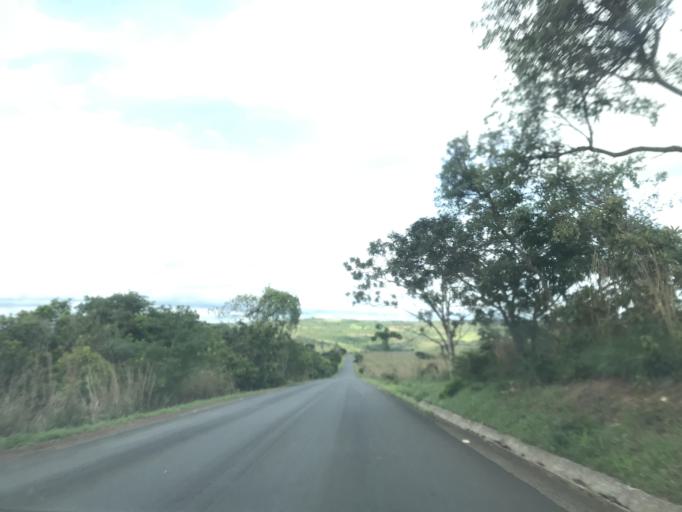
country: BR
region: Goias
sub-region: Vianopolis
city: Vianopolis
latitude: -16.9538
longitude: -48.5949
